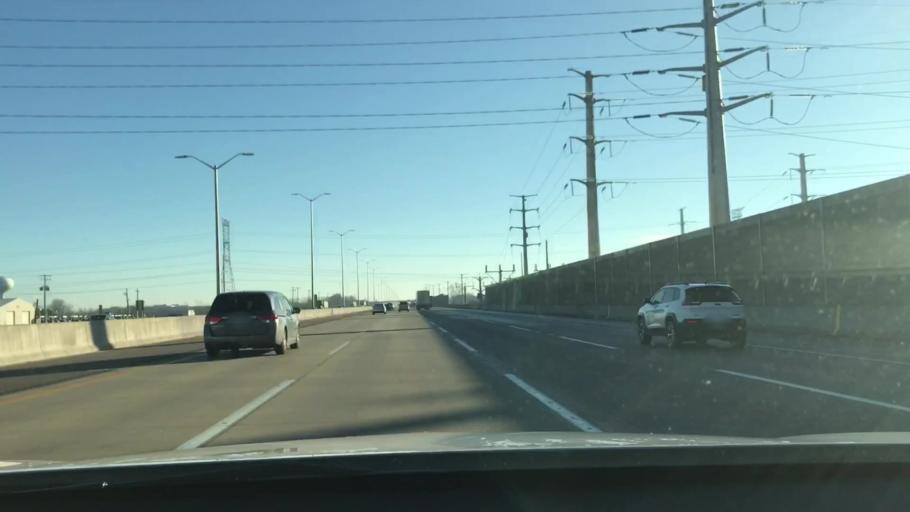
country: US
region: Illinois
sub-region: Kane County
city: East Dundee
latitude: 42.0672
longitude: -88.2428
